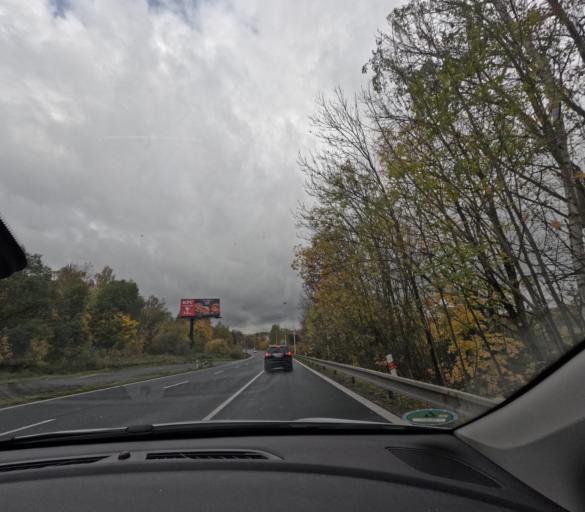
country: CZ
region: Karlovarsky
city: Dalovice
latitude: 50.2382
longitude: 12.8955
